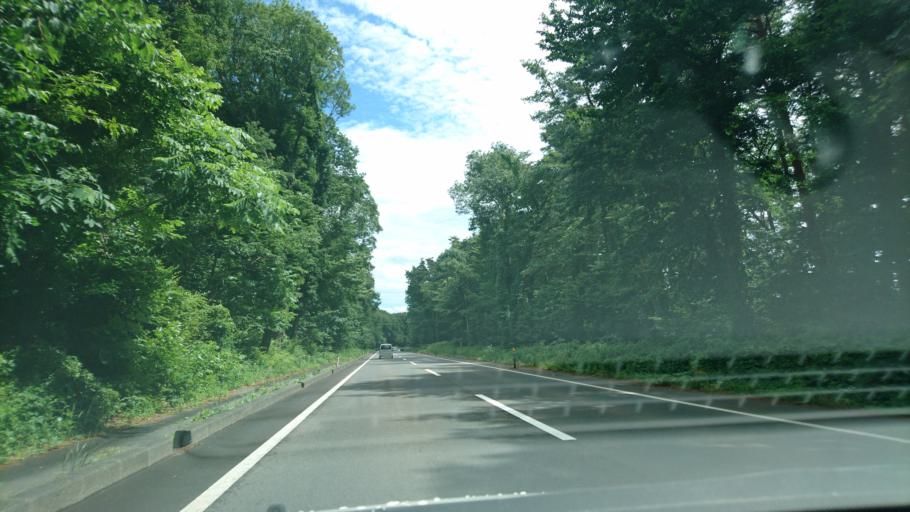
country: JP
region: Iwate
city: Morioka-shi
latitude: 39.7876
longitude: 141.1238
